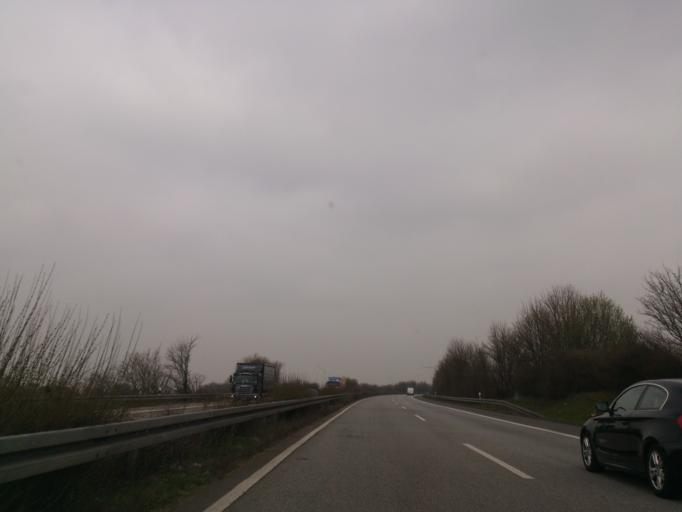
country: DE
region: North Rhine-Westphalia
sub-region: Regierungsbezirk Dusseldorf
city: Schwalmtal
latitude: 51.2048
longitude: 6.3070
